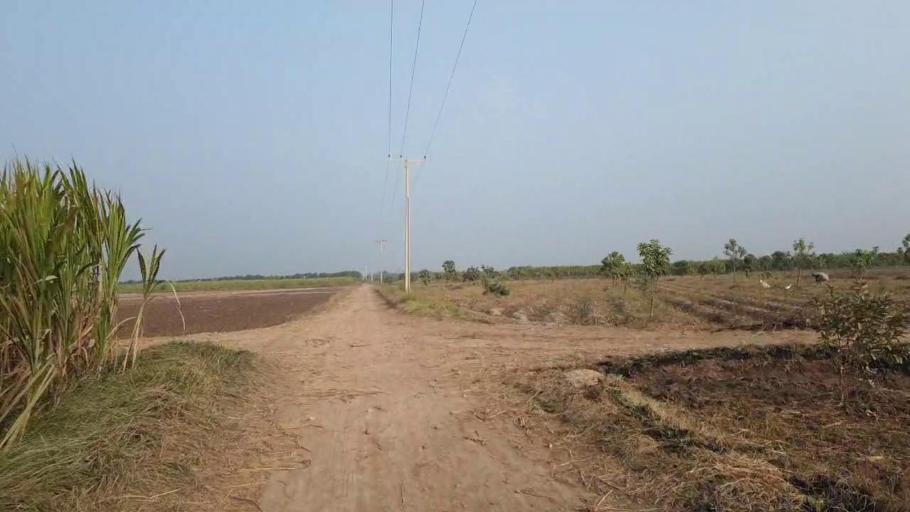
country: PK
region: Sindh
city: Tando Muhammad Khan
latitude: 25.1504
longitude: 68.5881
